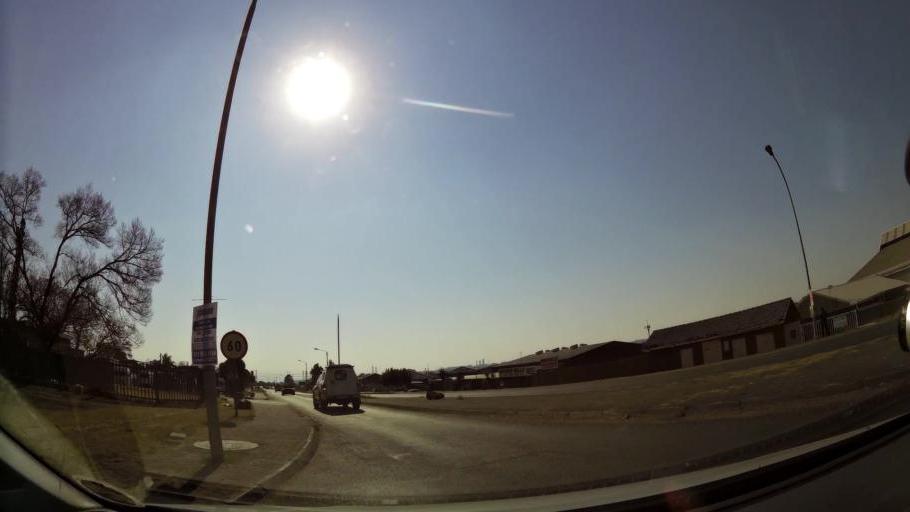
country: ZA
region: Gauteng
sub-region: City of Johannesburg Metropolitan Municipality
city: Modderfontein
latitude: -26.1243
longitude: 28.1733
